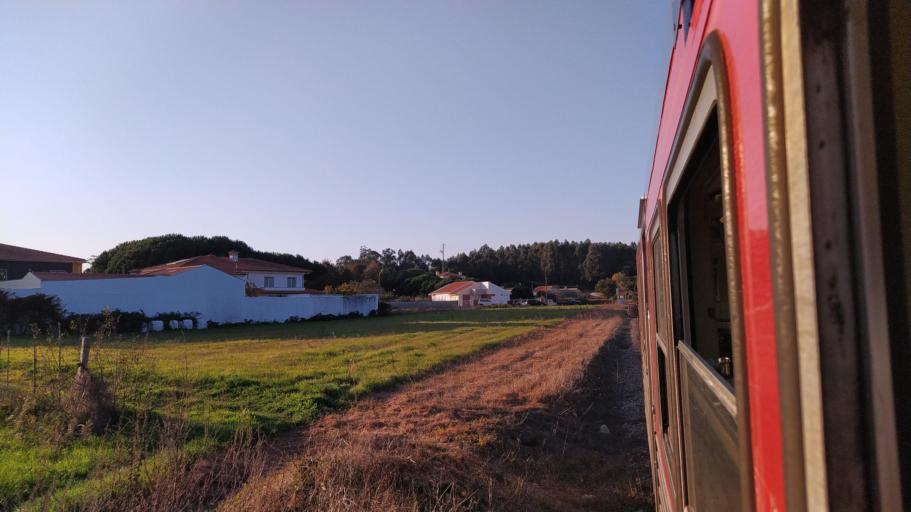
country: PT
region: Aveiro
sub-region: Aveiro
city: Eixo
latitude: 40.6385
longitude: -8.5846
